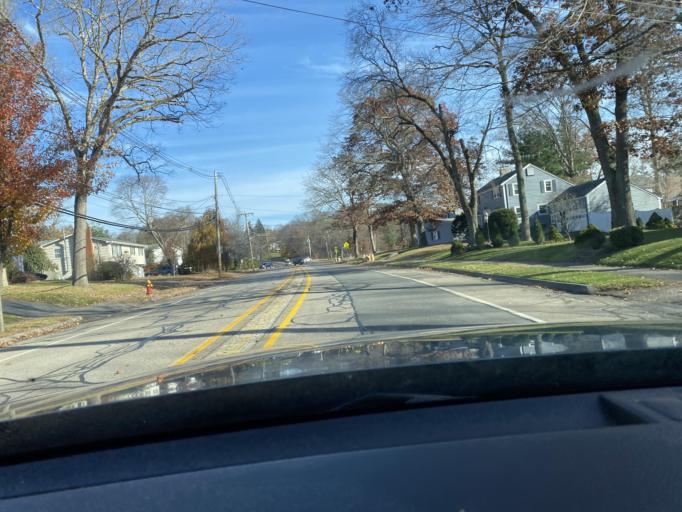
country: US
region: Massachusetts
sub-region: Norfolk County
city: Norwood
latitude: 42.1843
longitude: -71.2229
